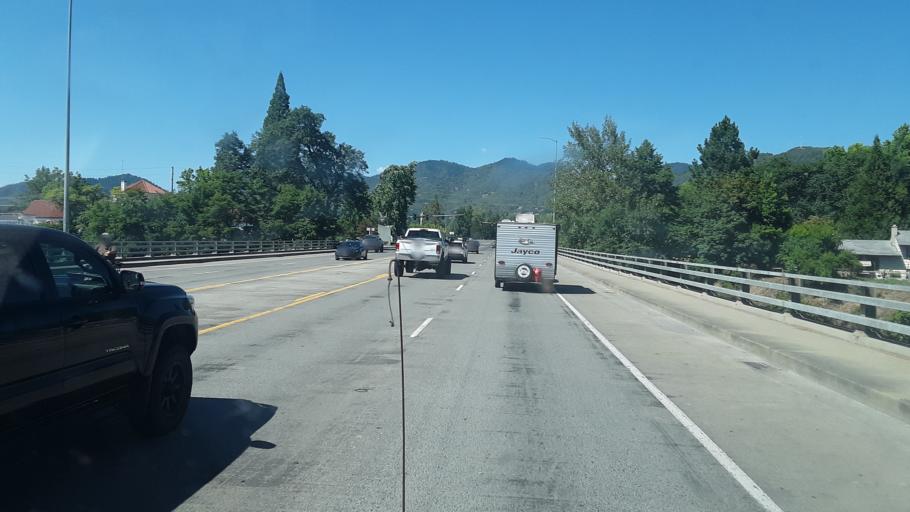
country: US
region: Oregon
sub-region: Josephine County
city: Fruitdale
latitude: 42.4290
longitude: -123.3186
